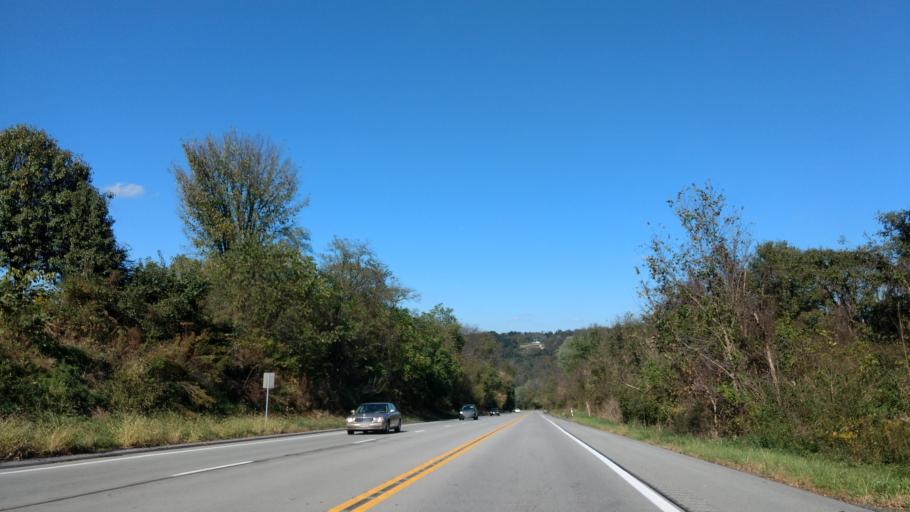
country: US
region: Pennsylvania
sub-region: Washington County
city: Wickerham Manor-Fisher
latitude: 40.1886
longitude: -79.9154
